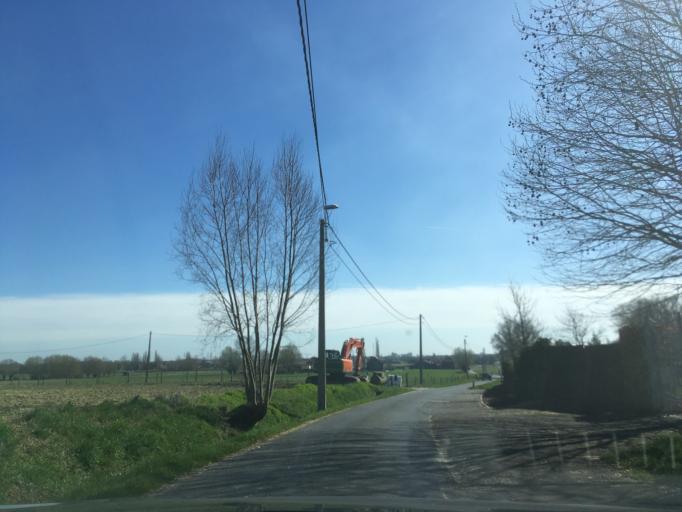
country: BE
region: Flanders
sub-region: Provincie West-Vlaanderen
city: Hooglede
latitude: 50.9806
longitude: 3.0995
